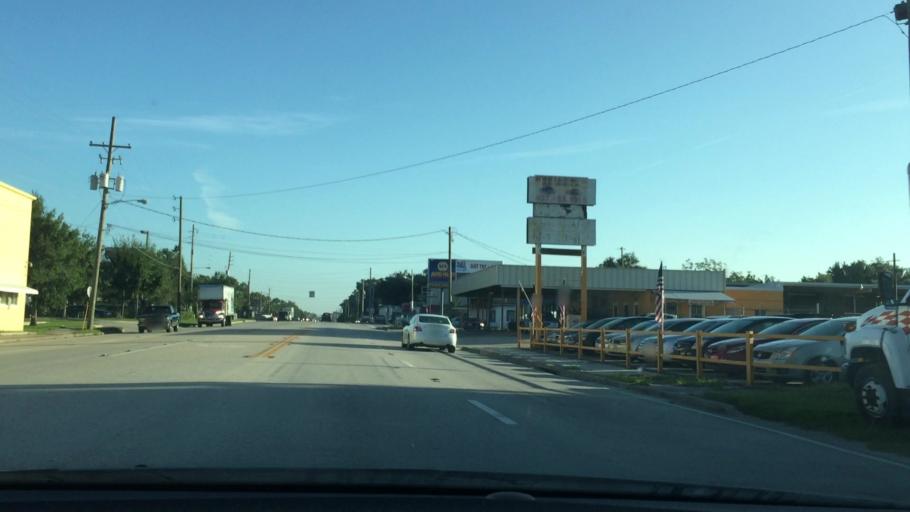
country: US
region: Florida
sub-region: Osceola County
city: Kissimmee
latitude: 28.3106
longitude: -81.4037
